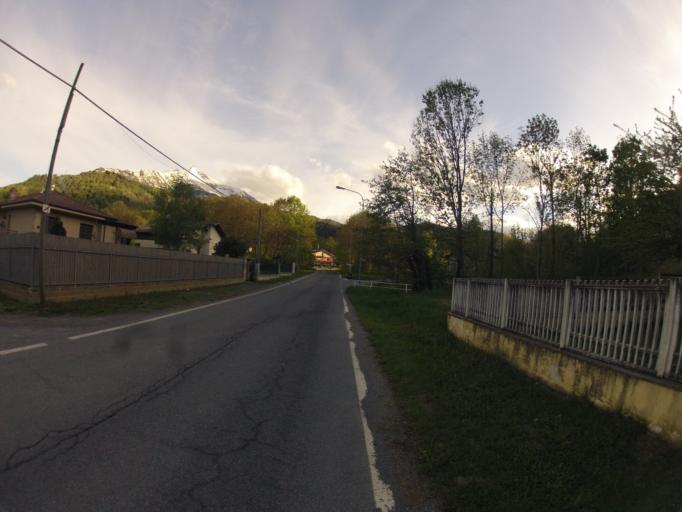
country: IT
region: Piedmont
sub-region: Provincia di Cuneo
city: Peveragno
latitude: 44.3211
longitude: 7.5990
